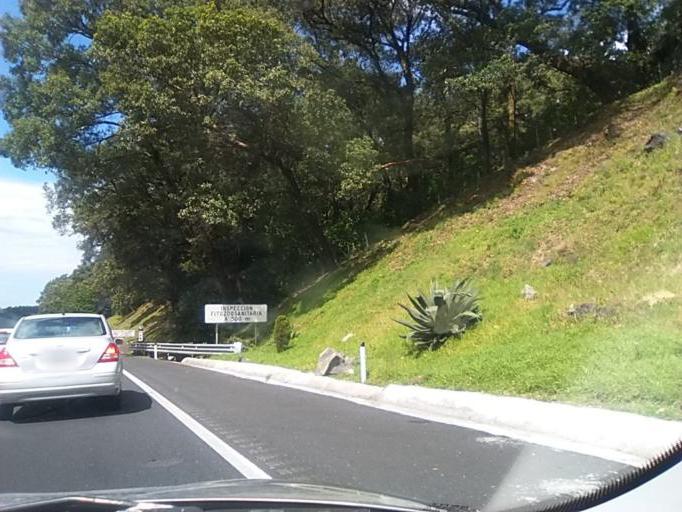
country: MX
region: Morelos
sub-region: Cuernavaca
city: Villa Santiago
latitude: 19.0145
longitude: -99.1559
